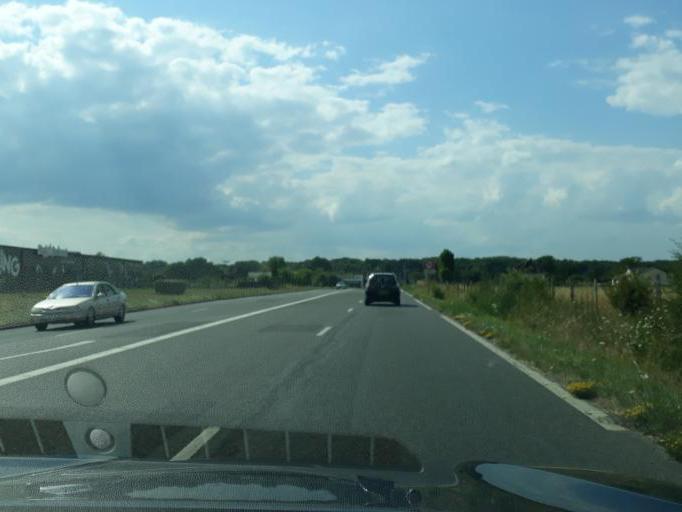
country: FR
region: Bourgogne
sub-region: Departement de la Nievre
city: Marzy
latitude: 47.0000
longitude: 3.1039
